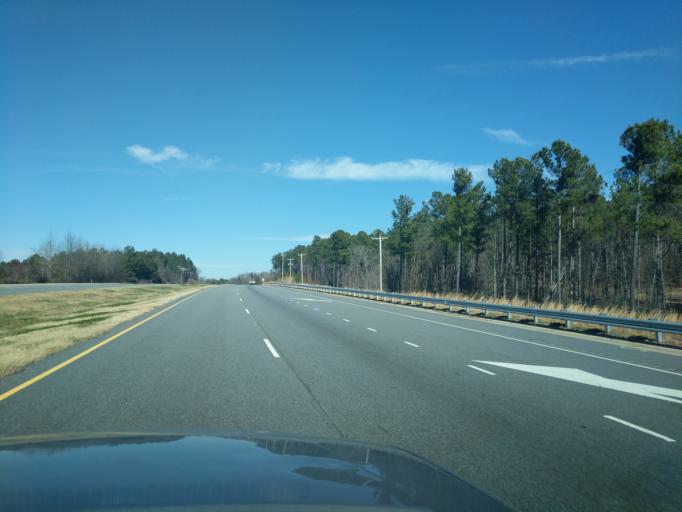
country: US
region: North Carolina
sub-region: Rutherford County
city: Forest City
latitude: 35.2131
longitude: -81.8396
